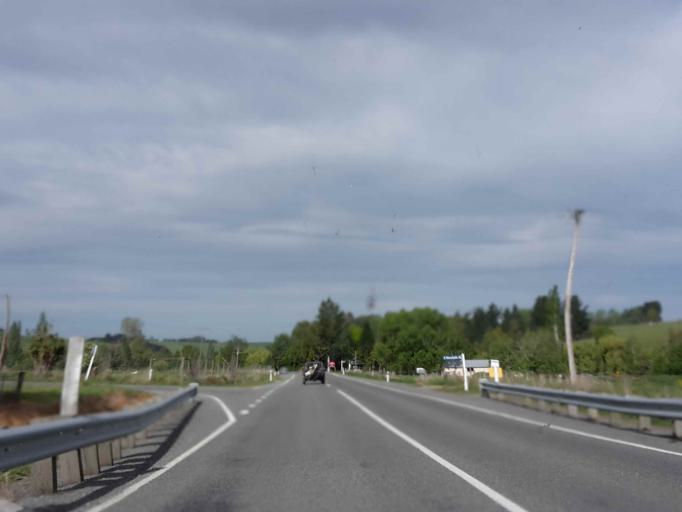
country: NZ
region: Canterbury
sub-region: Timaru District
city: Pleasant Point
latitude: -44.1115
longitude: 171.1434
